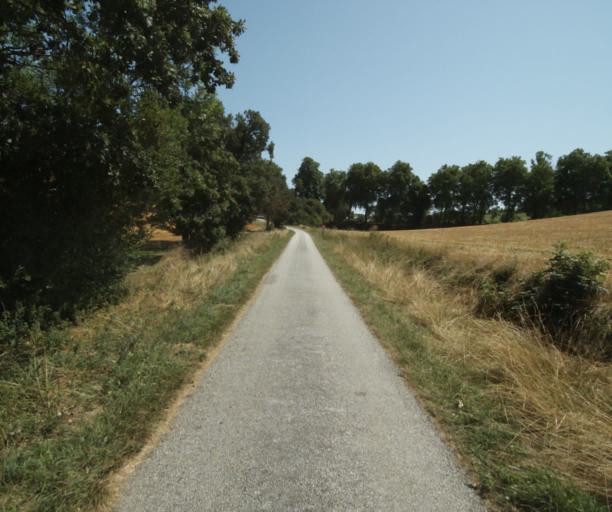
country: FR
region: Midi-Pyrenees
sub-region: Departement de la Haute-Garonne
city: Saint-Felix-Lauragais
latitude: 43.4628
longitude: 1.8569
